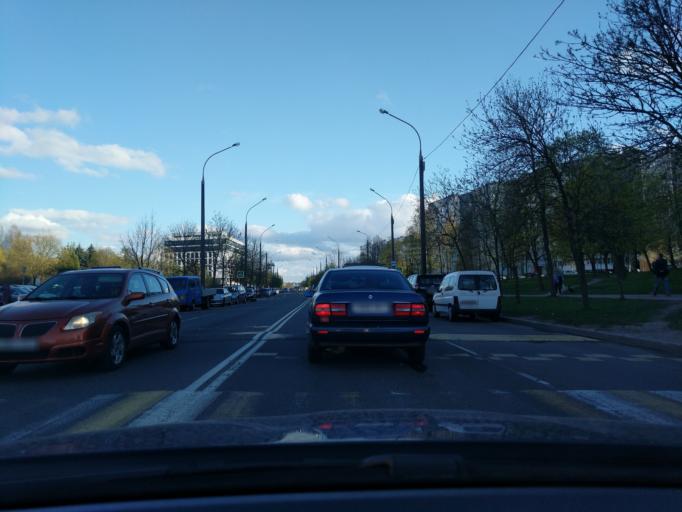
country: BY
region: Minsk
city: Novoye Medvezhino
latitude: 53.9118
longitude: 27.4511
